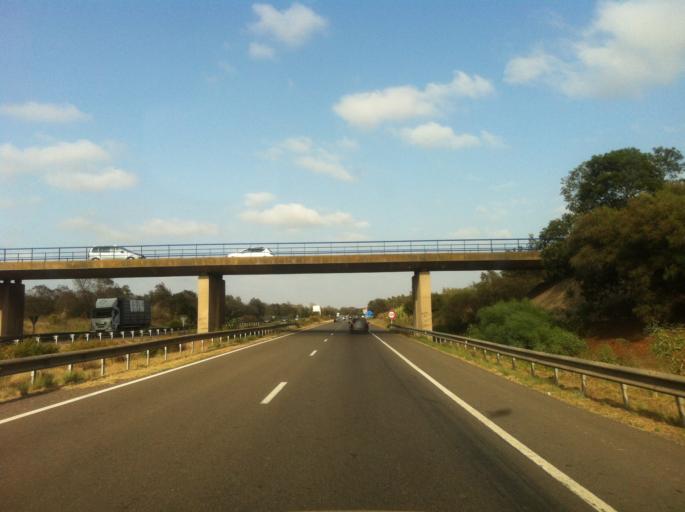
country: MA
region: Gharb-Chrarda-Beni Hssen
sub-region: Kenitra Province
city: Kenitra
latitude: 34.2289
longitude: -6.5804
